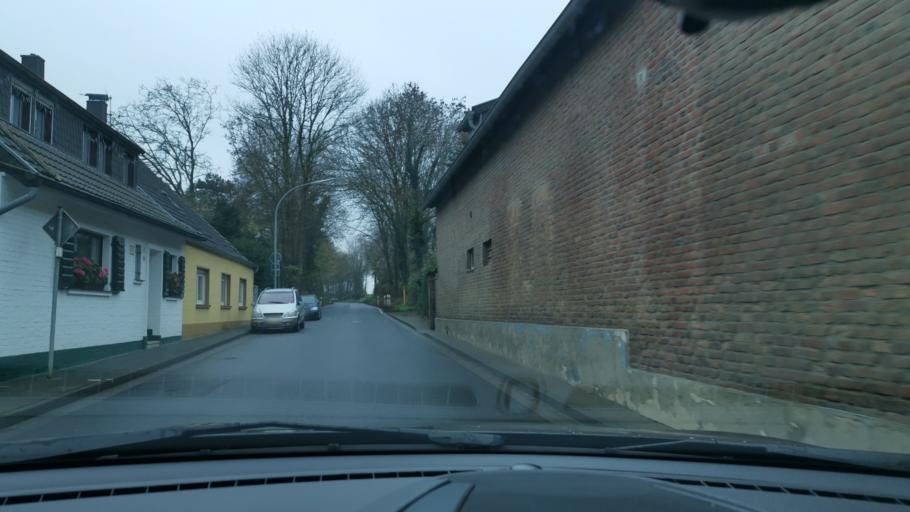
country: DE
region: North Rhine-Westphalia
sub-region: Regierungsbezirk Dusseldorf
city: Juchen
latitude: 51.1155
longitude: 6.5005
